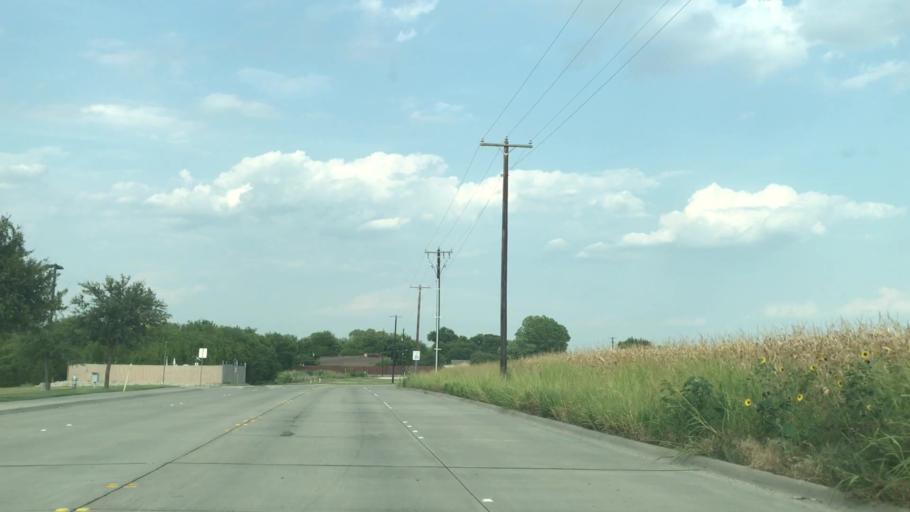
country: US
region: Texas
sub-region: Rockwall County
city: Rockwall
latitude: 32.9259
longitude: -96.4299
